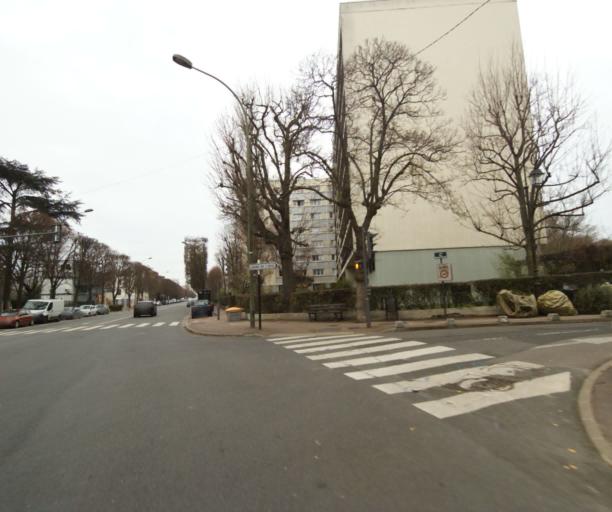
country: FR
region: Ile-de-France
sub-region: Departement des Hauts-de-Seine
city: Saint-Cloud
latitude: 48.8569
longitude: 2.2111
